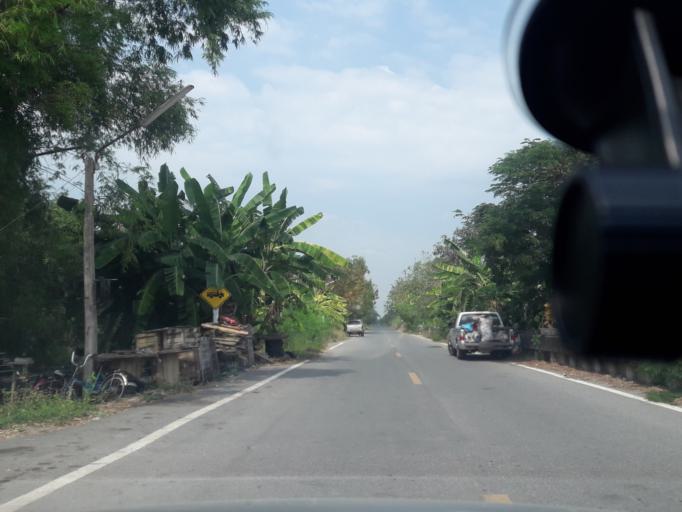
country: TH
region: Pathum Thani
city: Nong Suea
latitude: 14.2255
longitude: 100.8914
